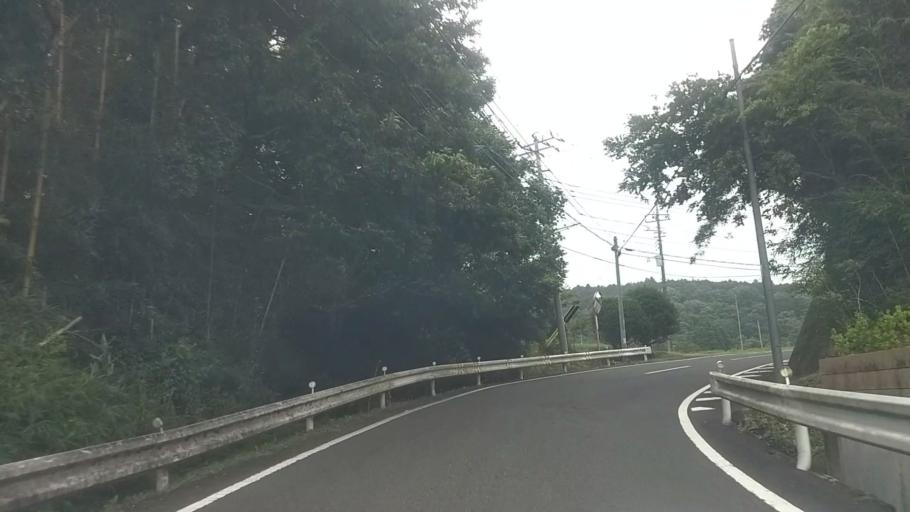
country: JP
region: Chiba
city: Kawaguchi
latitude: 35.2592
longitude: 140.0508
